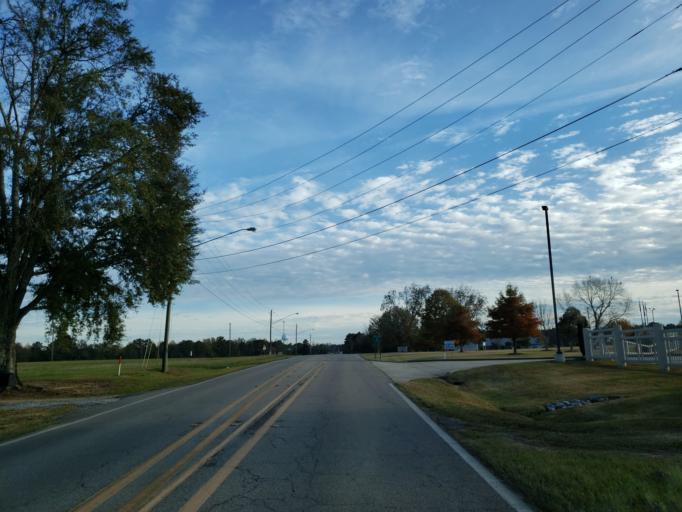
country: US
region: Mississippi
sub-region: Lamar County
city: Purvis
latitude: 31.1676
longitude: -89.4246
